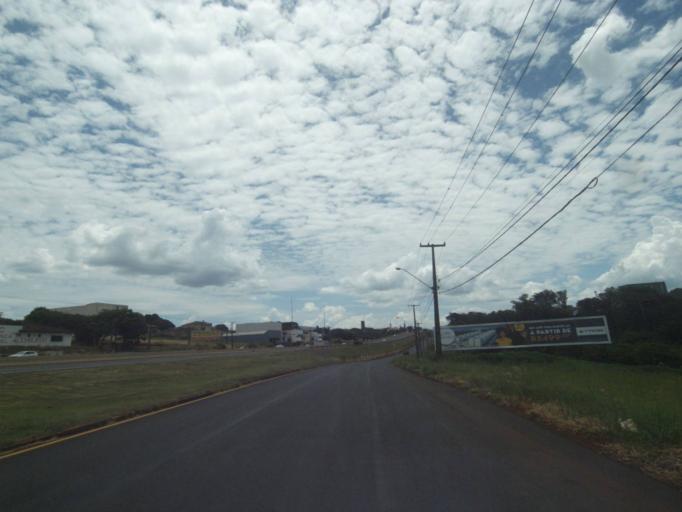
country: BR
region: Parana
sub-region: Londrina
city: Londrina
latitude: -23.3198
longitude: -51.2078
